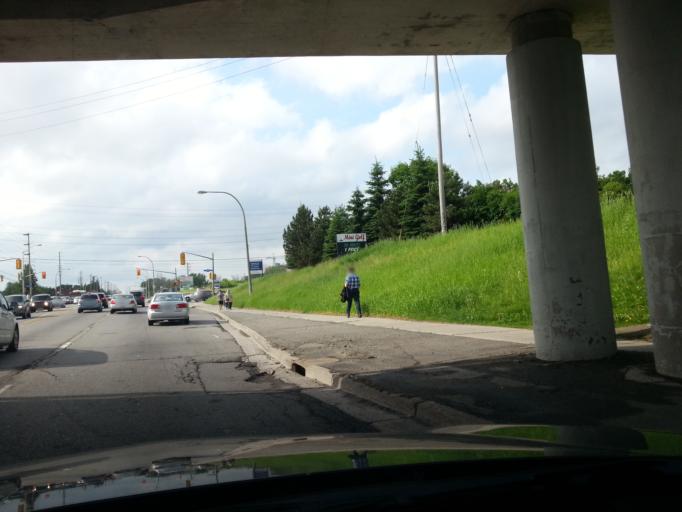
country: CA
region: Ontario
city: Ottawa
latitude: 45.3394
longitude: -75.7267
